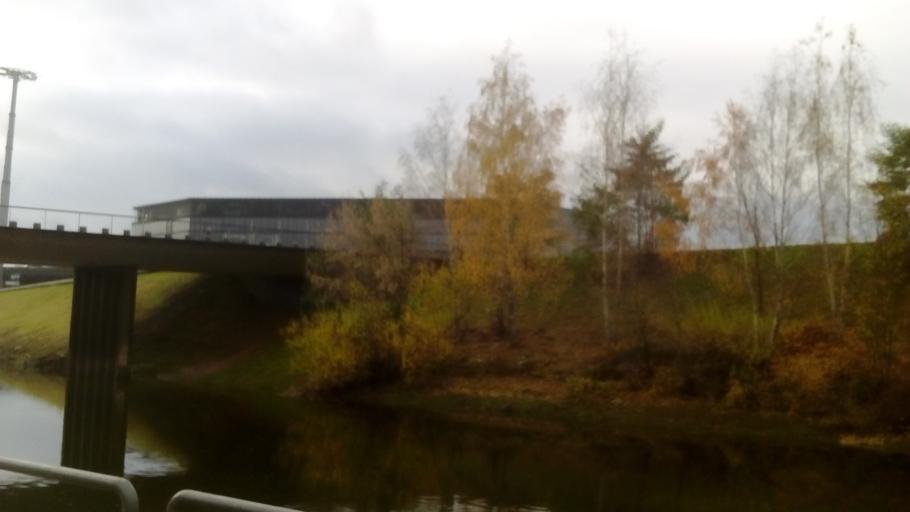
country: LT
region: Kauno apskritis
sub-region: Kaunas
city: Kaunas
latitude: 54.8928
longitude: 23.9151
